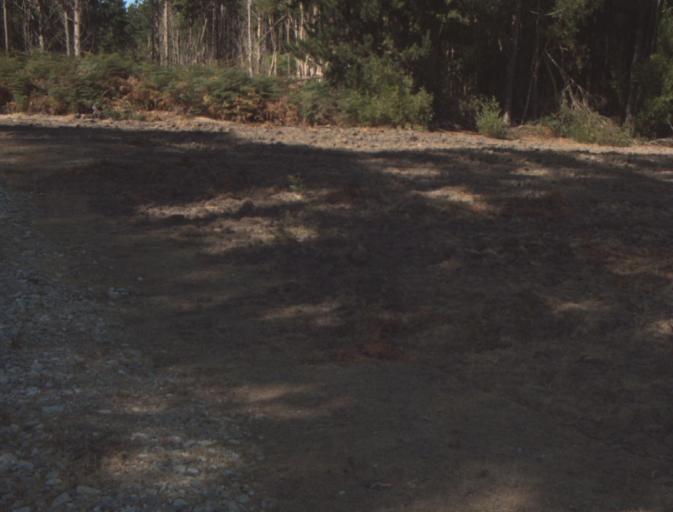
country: AU
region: Tasmania
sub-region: Launceston
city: Mayfield
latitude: -41.1581
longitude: 147.2060
